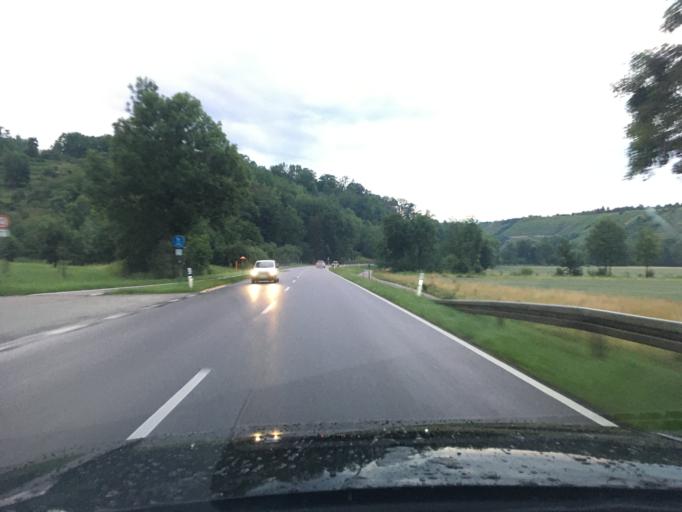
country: DE
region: Baden-Wuerttemberg
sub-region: Regierungsbezirk Stuttgart
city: Besigheim
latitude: 48.9787
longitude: 9.1446
